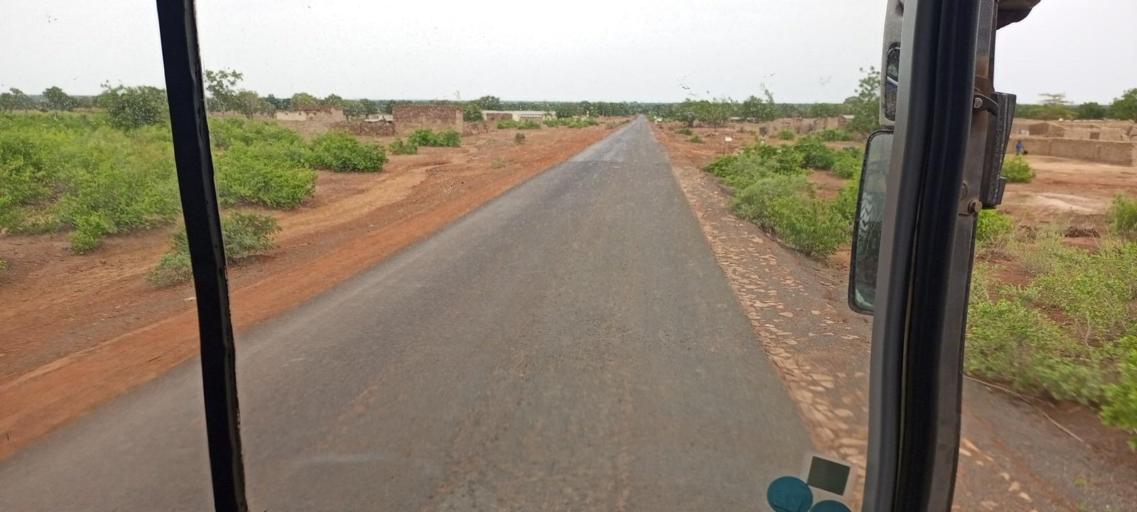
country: ML
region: Segou
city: Bla
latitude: 12.6899
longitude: -5.7237
